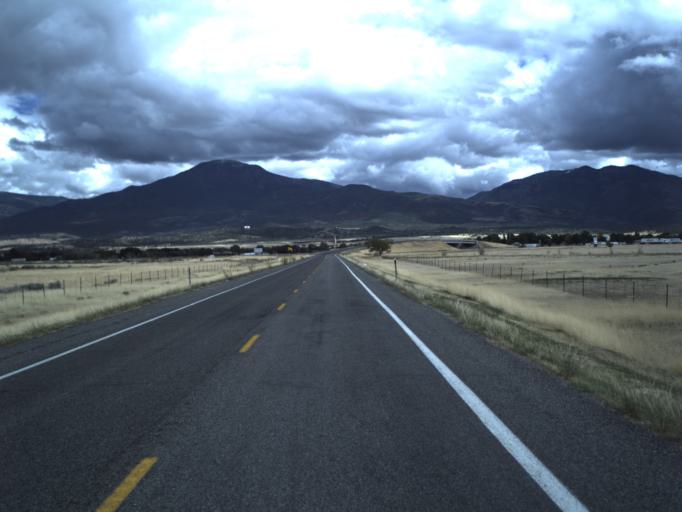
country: US
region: Utah
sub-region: Millard County
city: Fillmore
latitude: 38.9792
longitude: -112.3468
